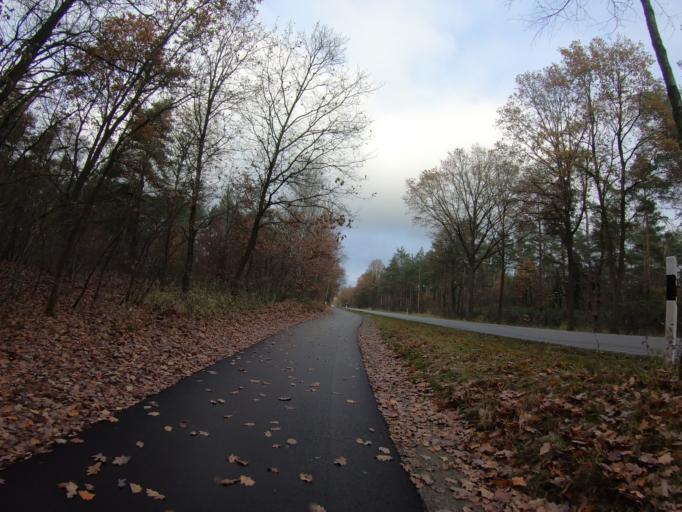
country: DE
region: Lower Saxony
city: Wesendorf
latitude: 52.5776
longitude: 10.5255
